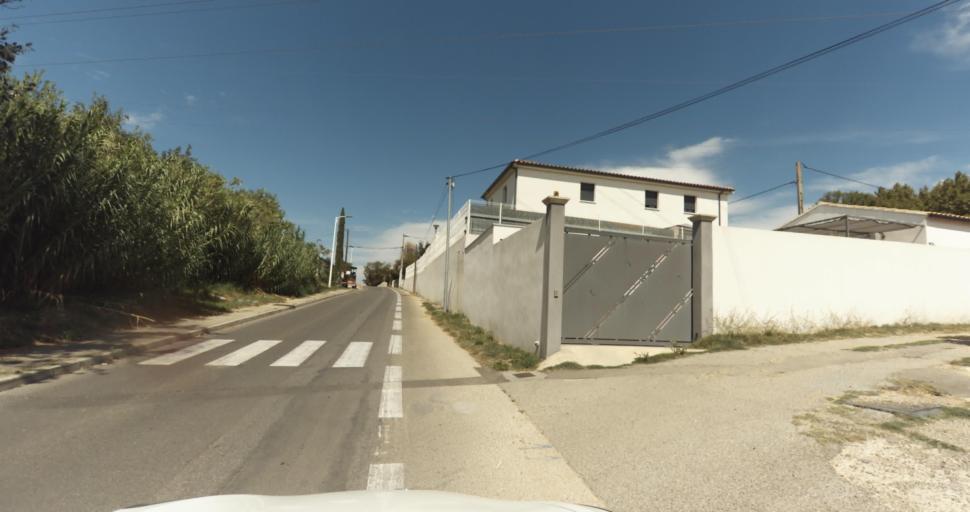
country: FR
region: Provence-Alpes-Cote d'Azur
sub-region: Departement des Bouches-du-Rhone
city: Miramas
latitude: 43.5792
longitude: 5.0146
